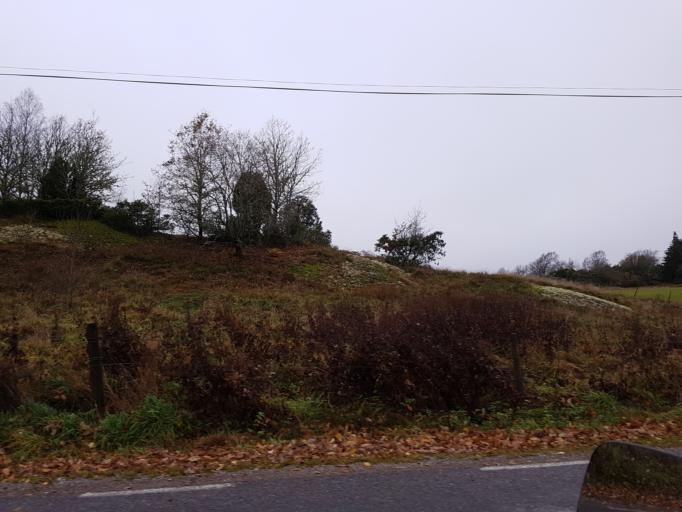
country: SE
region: Vaestra Goetaland
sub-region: Orust
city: Henan
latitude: 58.1652
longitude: 11.7232
